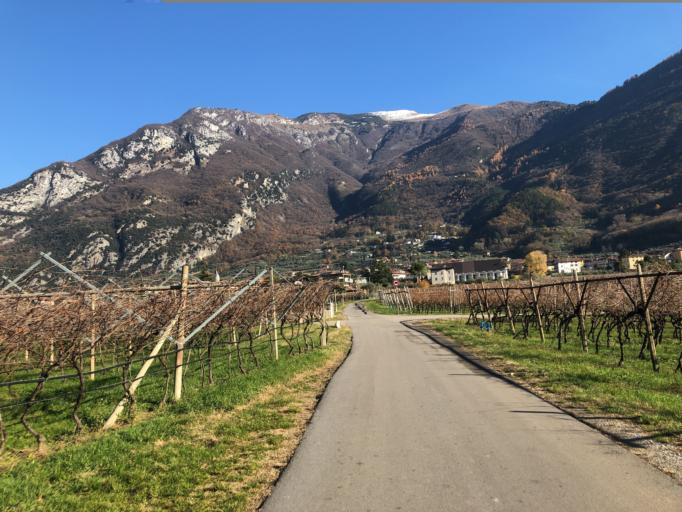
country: IT
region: Trentino-Alto Adige
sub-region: Provincia di Trento
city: Bolognano-Vignole
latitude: 45.9098
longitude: 10.8954
